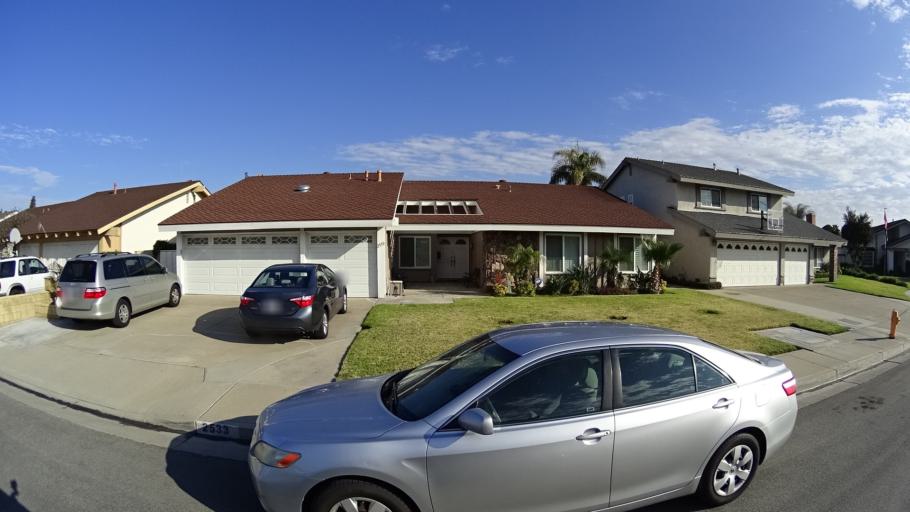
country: US
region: California
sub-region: Orange County
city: Anaheim
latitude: 33.8294
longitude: -117.8791
